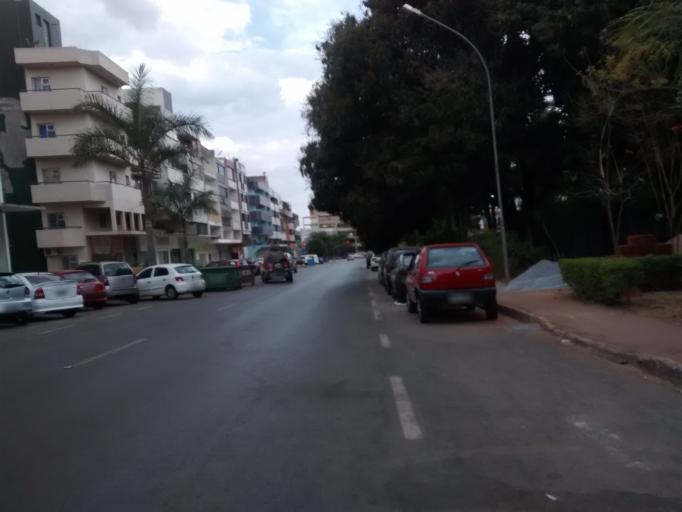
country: BR
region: Federal District
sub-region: Brasilia
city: Brasilia
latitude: -15.7396
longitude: -47.9010
